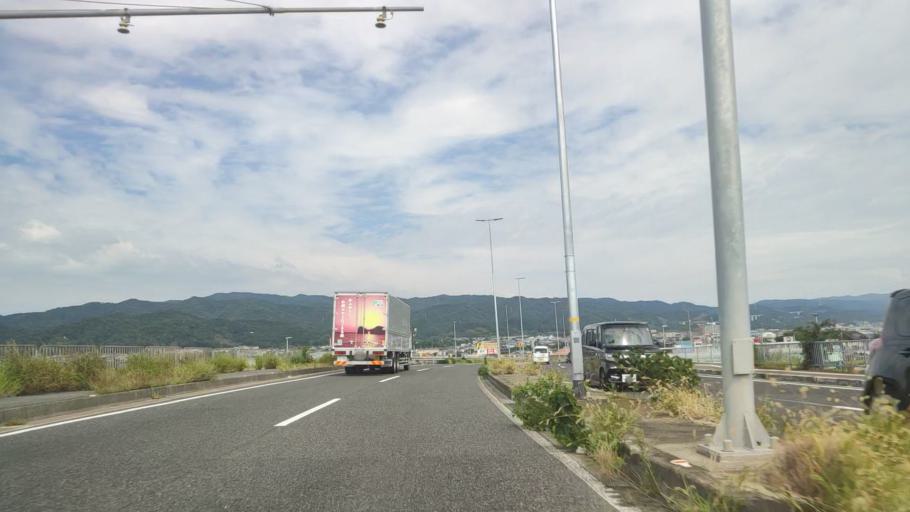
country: JP
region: Wakayama
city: Wakayama-shi
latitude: 34.2549
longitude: 135.2210
